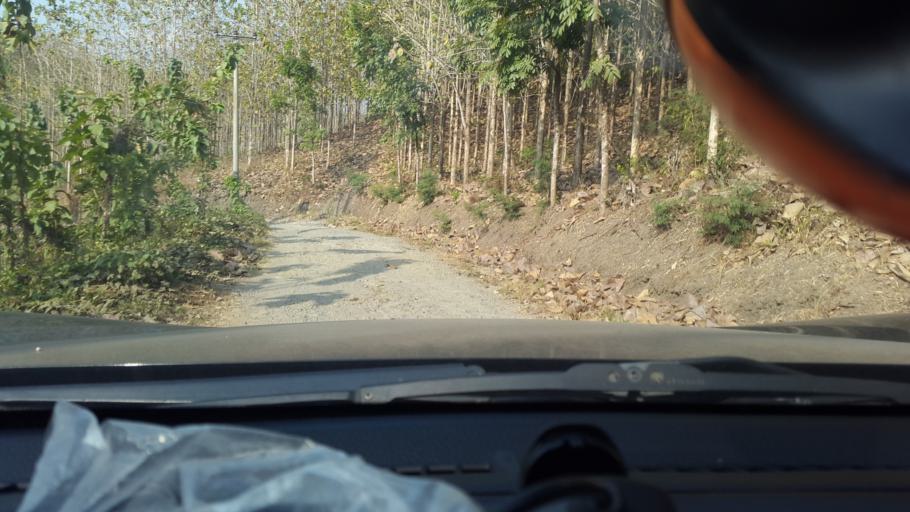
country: ID
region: West Java
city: Cikupa
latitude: -7.3598
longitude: 106.7020
